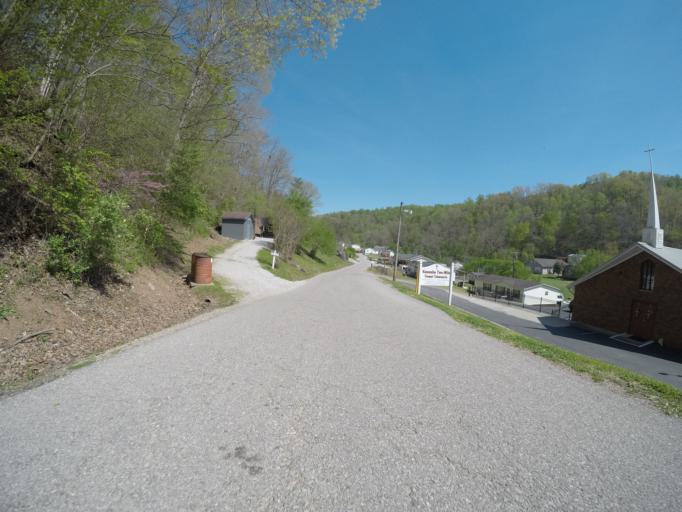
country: US
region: West Virginia
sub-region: Kanawha County
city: Charleston
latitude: 38.4141
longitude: -81.6117
